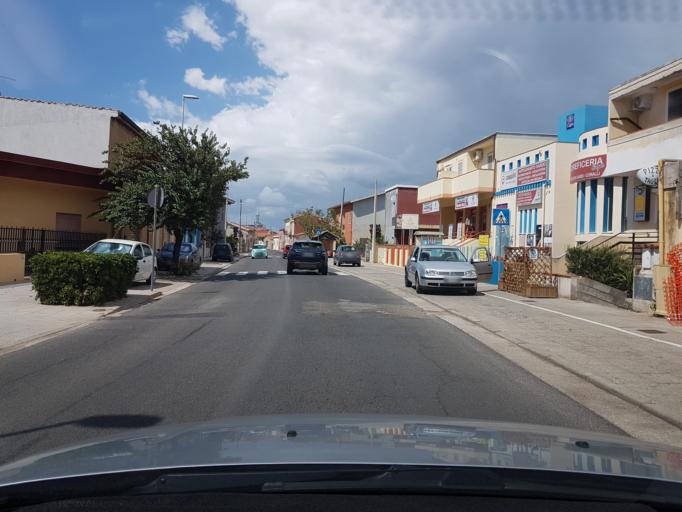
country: IT
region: Sardinia
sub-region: Provincia di Oristano
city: Riola Sardo
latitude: 39.9927
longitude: 8.5416
